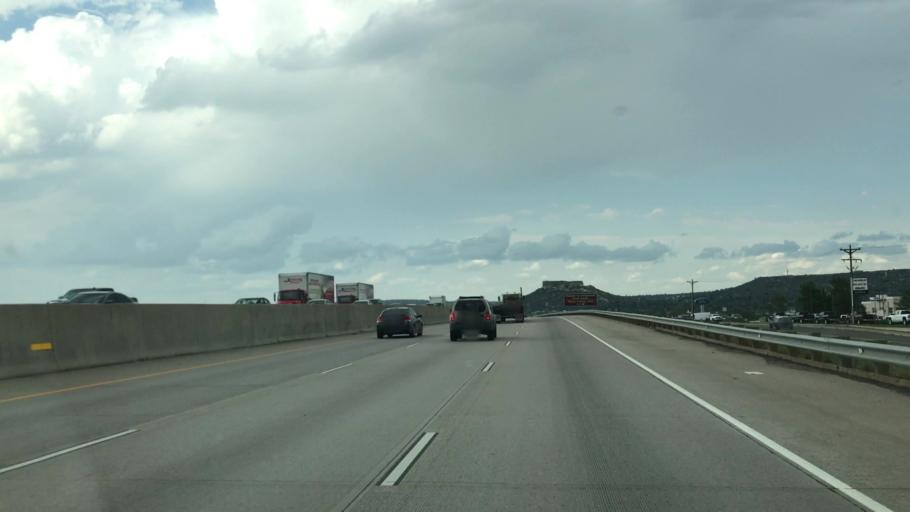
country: US
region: Colorado
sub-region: Douglas County
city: Castle Rock
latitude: 39.3553
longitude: -104.8693
